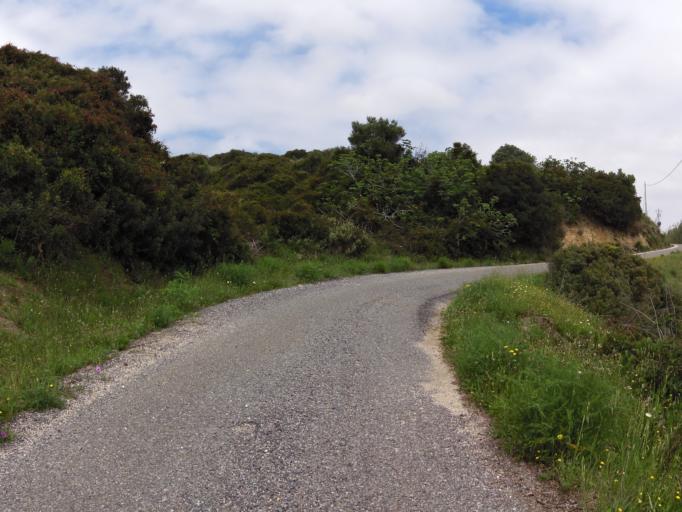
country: PT
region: Faro
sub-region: Vila do Bispo
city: Vila do Bispo
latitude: 37.0753
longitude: -8.8754
